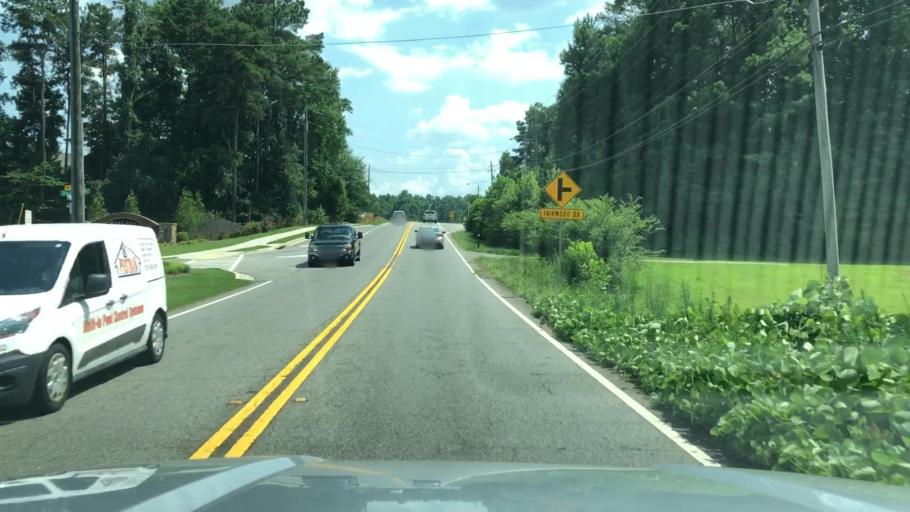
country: US
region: Georgia
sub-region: Cobb County
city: Acworth
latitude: 33.9822
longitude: -84.7160
